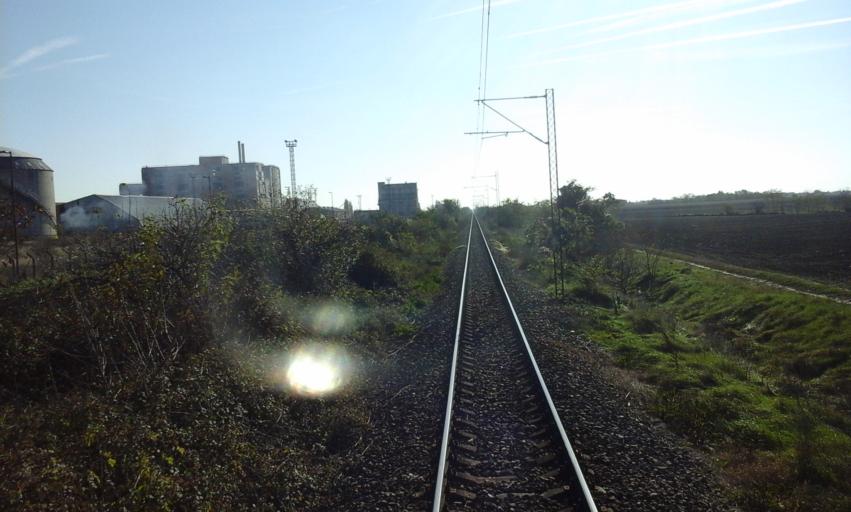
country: RS
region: Autonomna Pokrajina Vojvodina
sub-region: Severnobacki Okrug
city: Subotica
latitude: 46.0101
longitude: 19.6791
